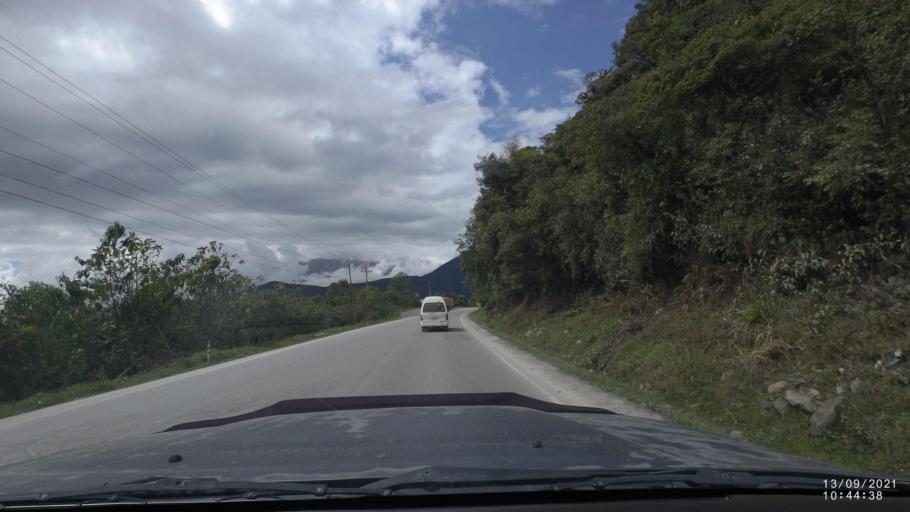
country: BO
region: Cochabamba
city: Colomi
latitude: -17.1946
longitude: -65.8775
